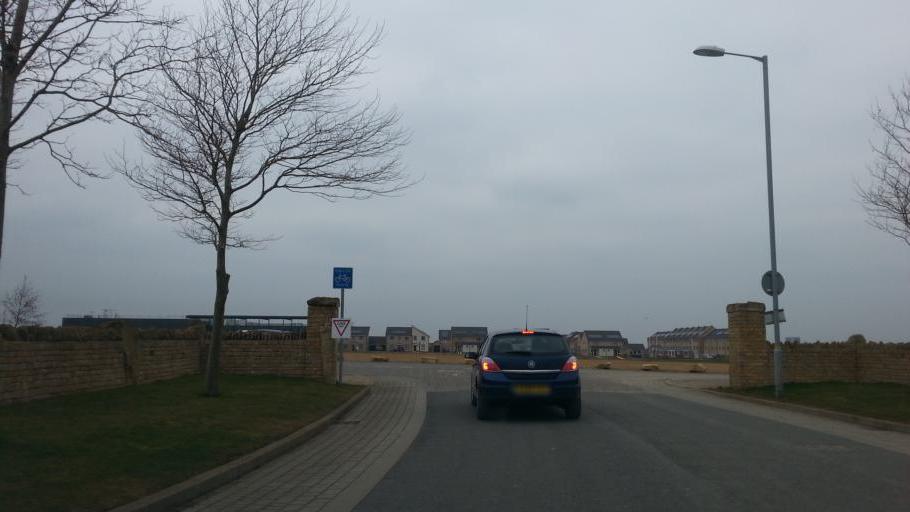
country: GB
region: England
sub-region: Northamptonshire
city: Corby
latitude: 52.5067
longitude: -0.6388
